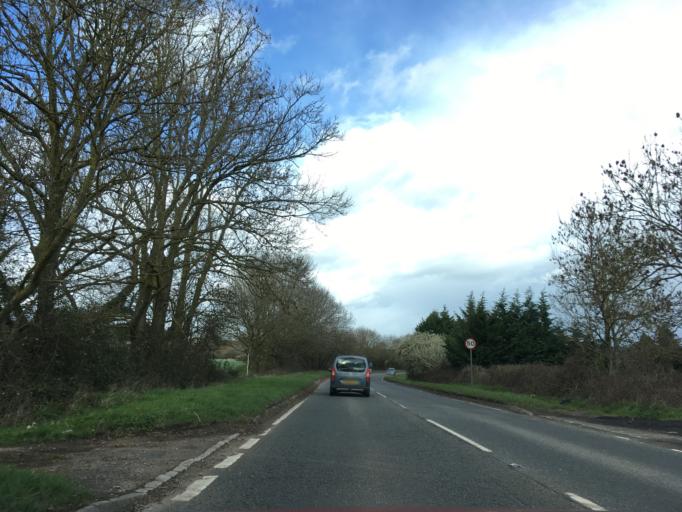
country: GB
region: England
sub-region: Gloucestershire
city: Cinderford
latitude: 51.8237
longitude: -2.4301
